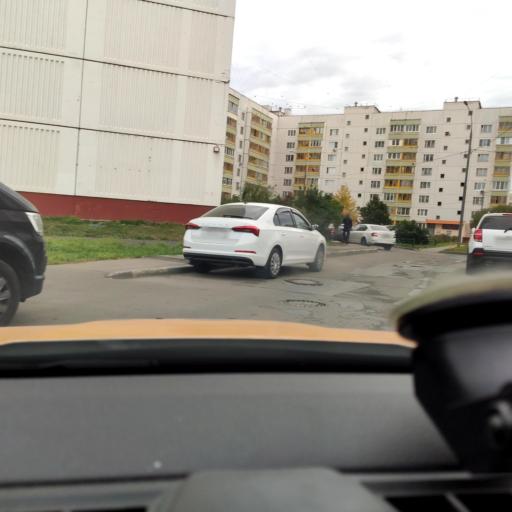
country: RU
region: Moscow
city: Kuz'minki
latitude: 55.6715
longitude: 37.7890
